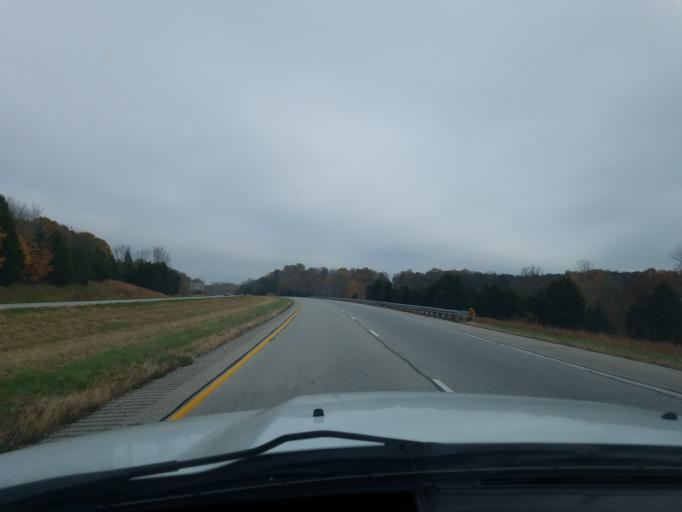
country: US
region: Indiana
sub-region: Harrison County
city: Corydon
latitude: 38.2438
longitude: -86.0954
